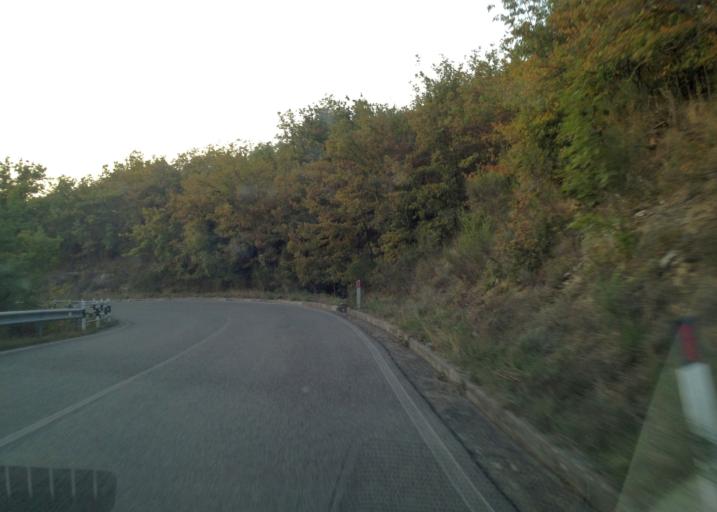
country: IT
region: Tuscany
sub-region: Provincia di Siena
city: Castellina in Chianti
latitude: 43.5045
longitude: 11.2934
